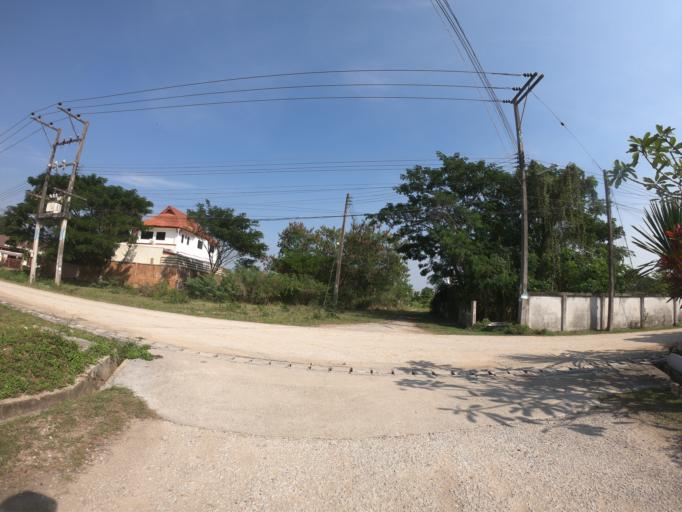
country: TH
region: Chiang Mai
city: Chiang Mai
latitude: 18.8243
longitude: 99.0059
